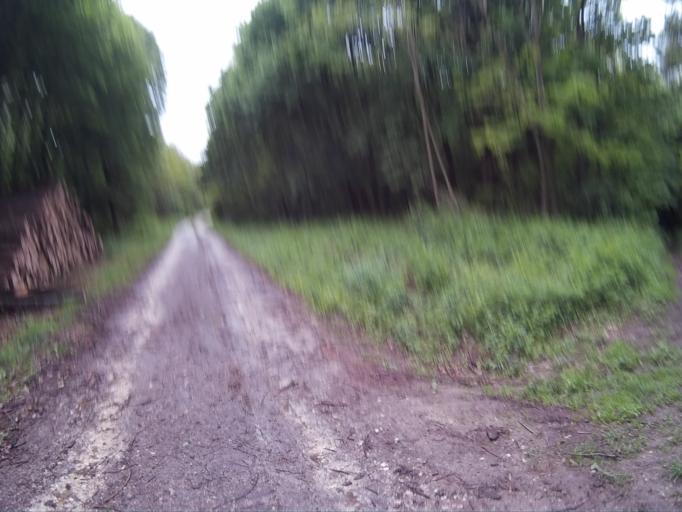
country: HU
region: Veszprem
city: Sumeg
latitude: 46.9058
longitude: 17.2700
